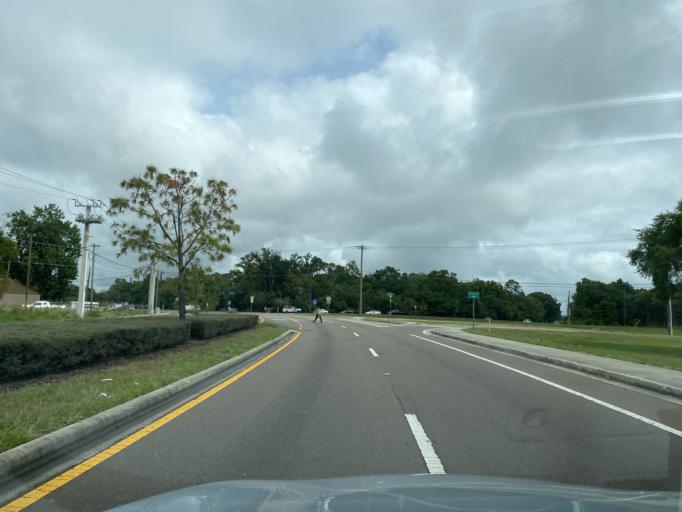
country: US
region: Florida
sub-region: Seminole County
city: Sanford
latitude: 28.7882
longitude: -81.2978
